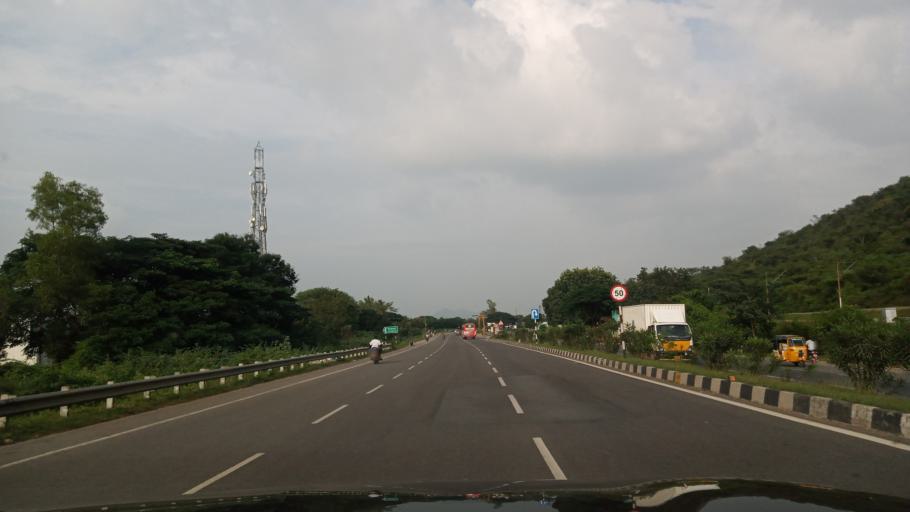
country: IN
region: Tamil Nadu
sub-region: Vellore
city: Ambur
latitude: 12.8085
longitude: 78.7401
